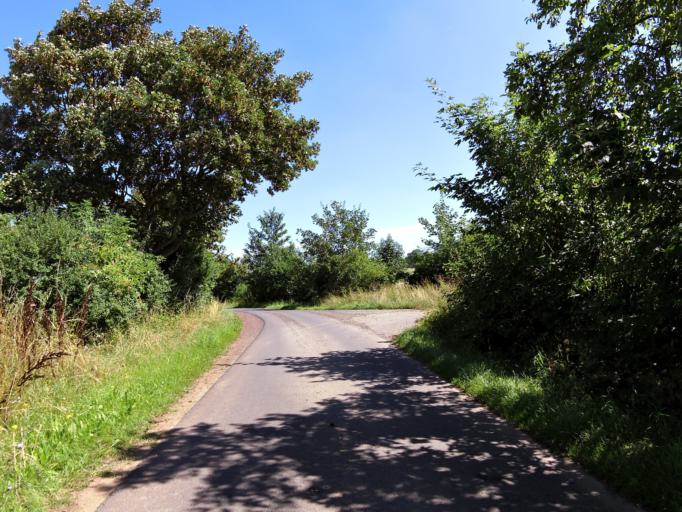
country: DE
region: Thuringia
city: Haina
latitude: 50.9673
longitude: 10.4617
